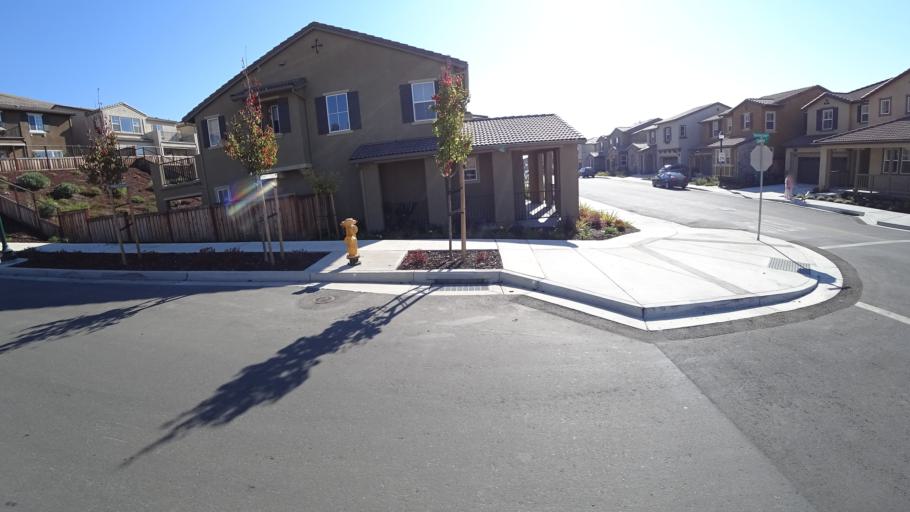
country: US
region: California
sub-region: Alameda County
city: Fairview
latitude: 37.6385
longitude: -122.0457
